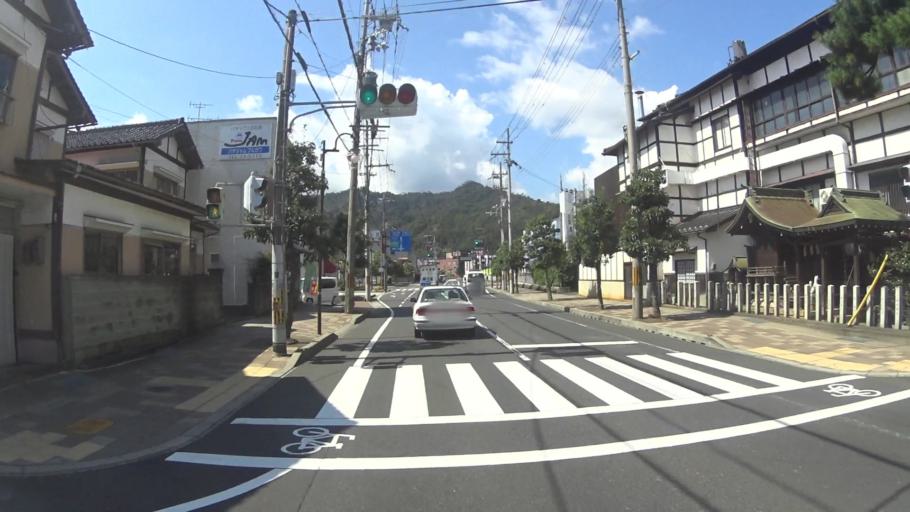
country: JP
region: Kyoto
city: Miyazu
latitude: 35.5376
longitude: 135.1951
